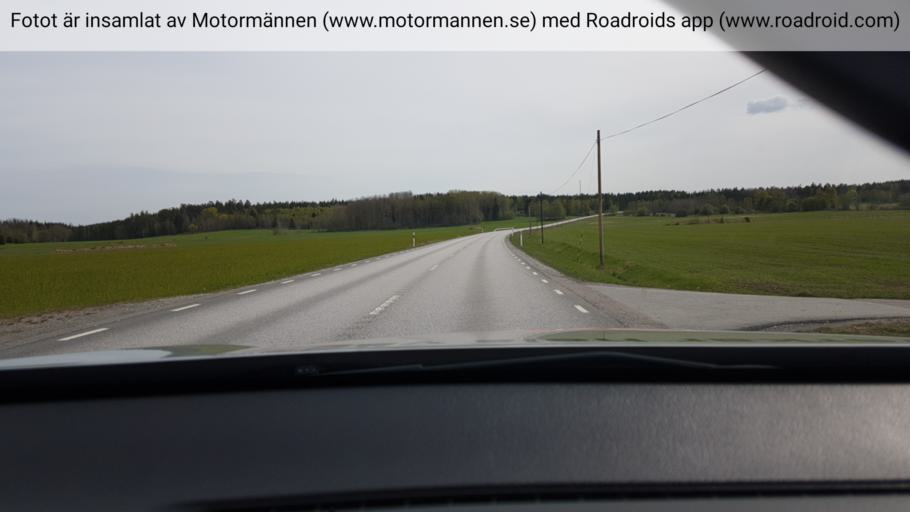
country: SE
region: Stockholm
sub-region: Vallentuna Kommun
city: Vallentuna
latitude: 59.7178
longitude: 18.0549
